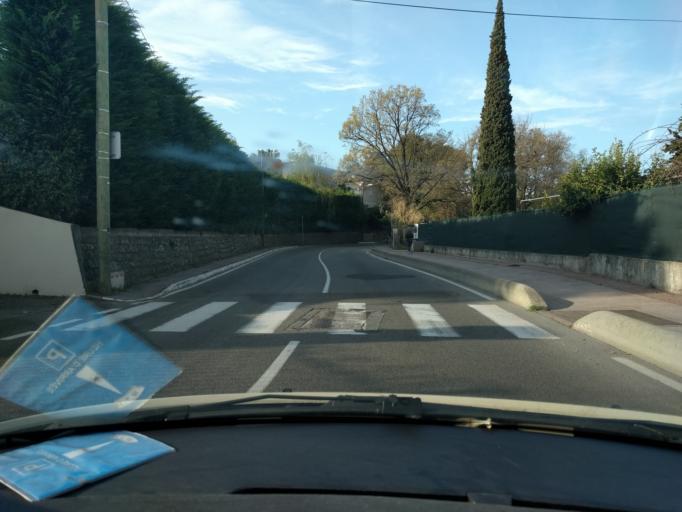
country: FR
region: Provence-Alpes-Cote d'Azur
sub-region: Departement des Alpes-Maritimes
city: Mougins
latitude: 43.5887
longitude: 6.9996
